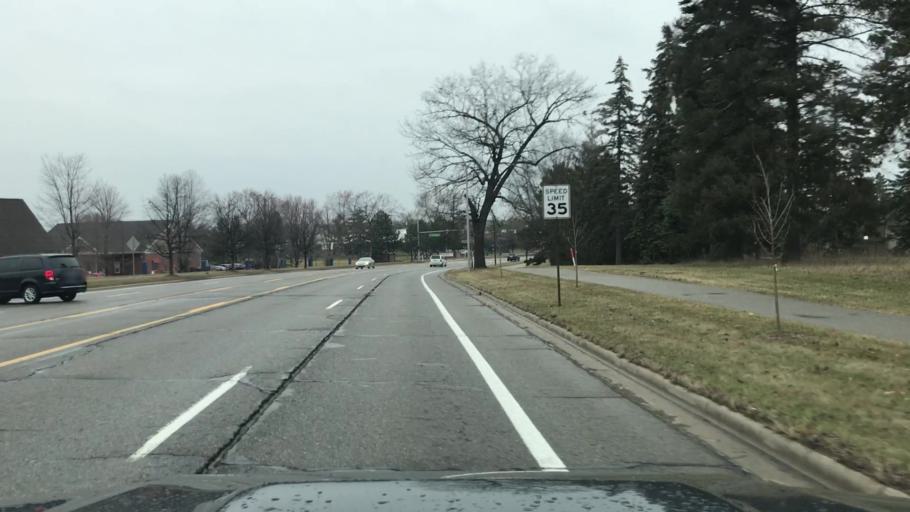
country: US
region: Michigan
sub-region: Washtenaw County
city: Ann Arbor
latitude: 42.3009
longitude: -83.7138
